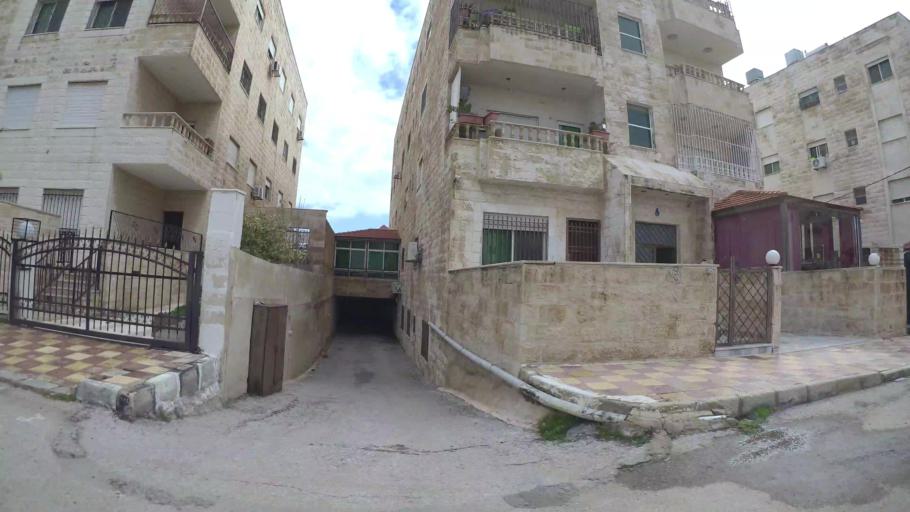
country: JO
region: Amman
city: Wadi as Sir
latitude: 31.9478
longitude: 35.8350
